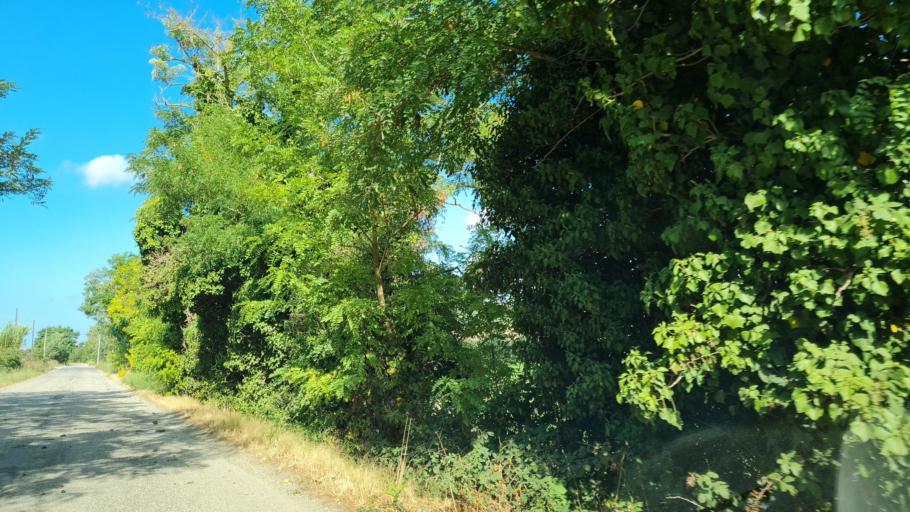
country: IT
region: Latium
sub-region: Provincia di Viterbo
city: Tarquinia
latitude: 42.2610
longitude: 11.7607
